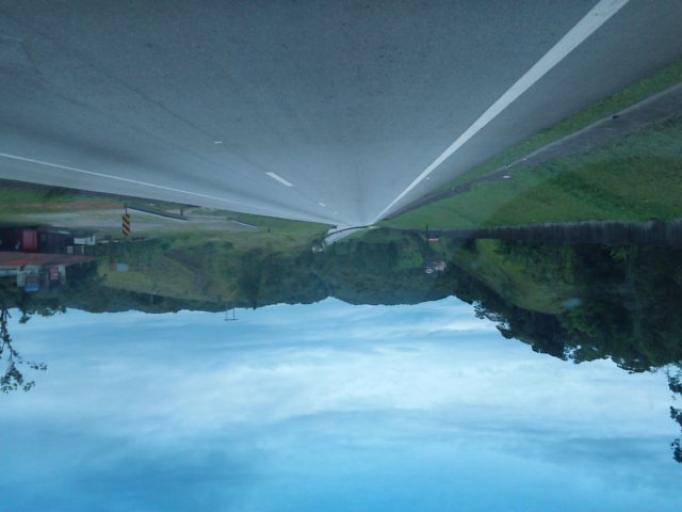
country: BR
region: Sao Paulo
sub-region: Juquitiba
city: Juquitiba
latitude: -24.0137
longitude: -47.1671
